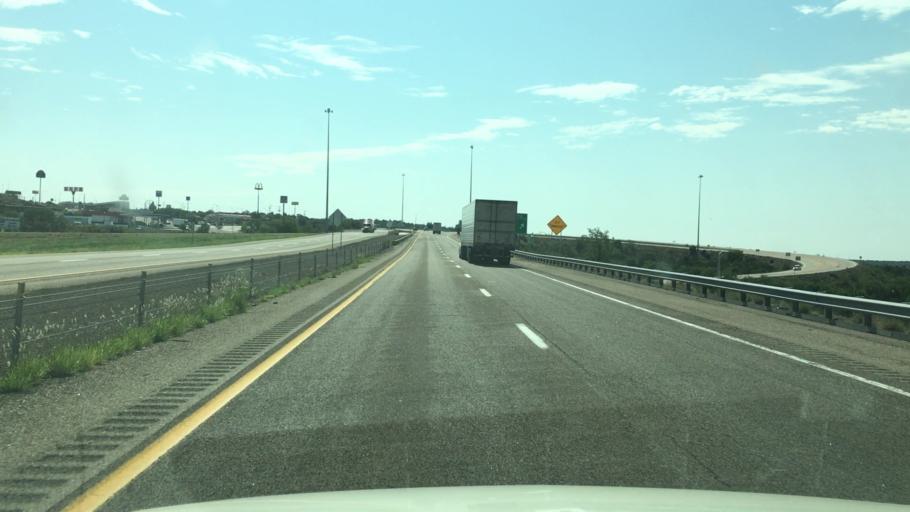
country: US
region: New Mexico
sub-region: Guadalupe County
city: Santa Rosa
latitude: 34.9460
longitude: -104.6758
